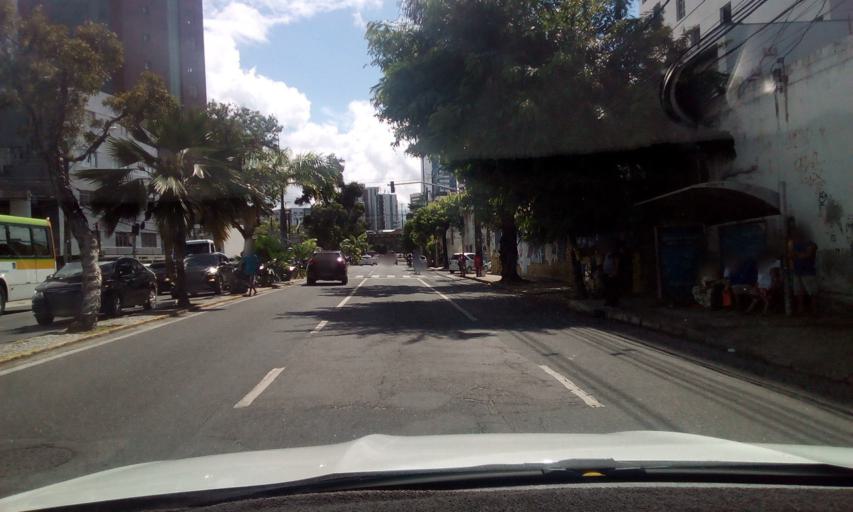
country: BR
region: Pernambuco
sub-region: Recife
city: Recife
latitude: -8.0472
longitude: -34.8898
